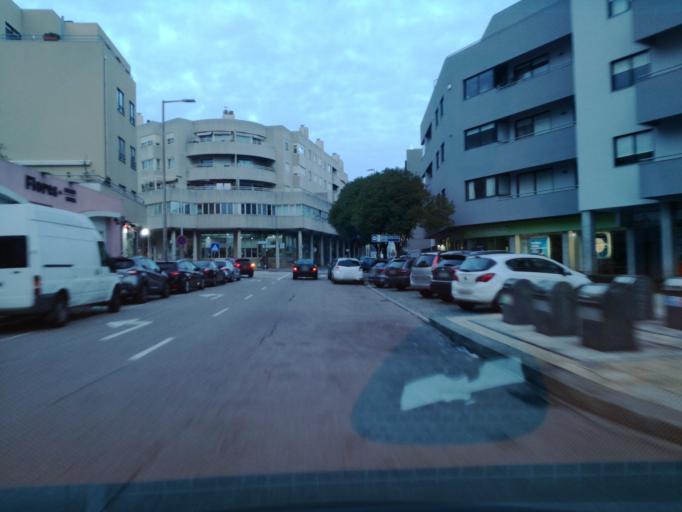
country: PT
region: Porto
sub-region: Vila Nova de Gaia
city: Canidelo
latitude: 41.1542
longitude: -8.6482
